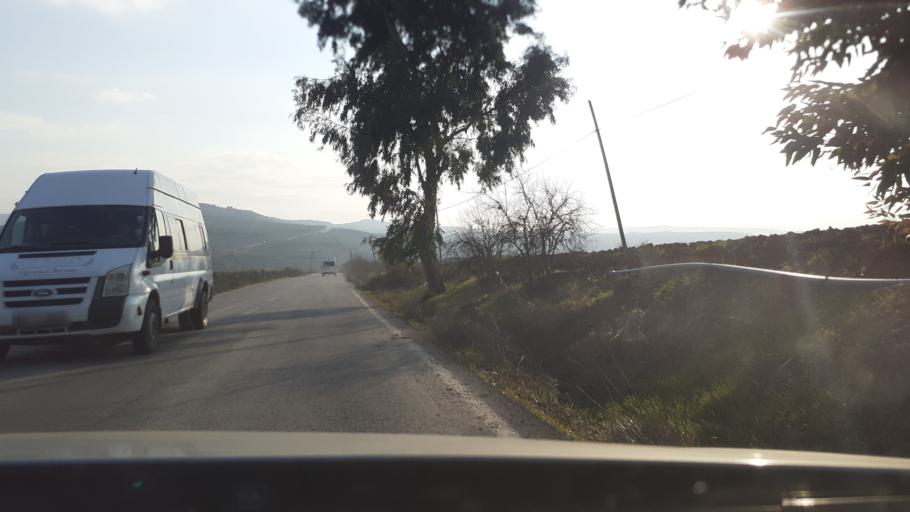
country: TR
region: Hatay
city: Oymakli
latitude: 36.1319
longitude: 36.3110
